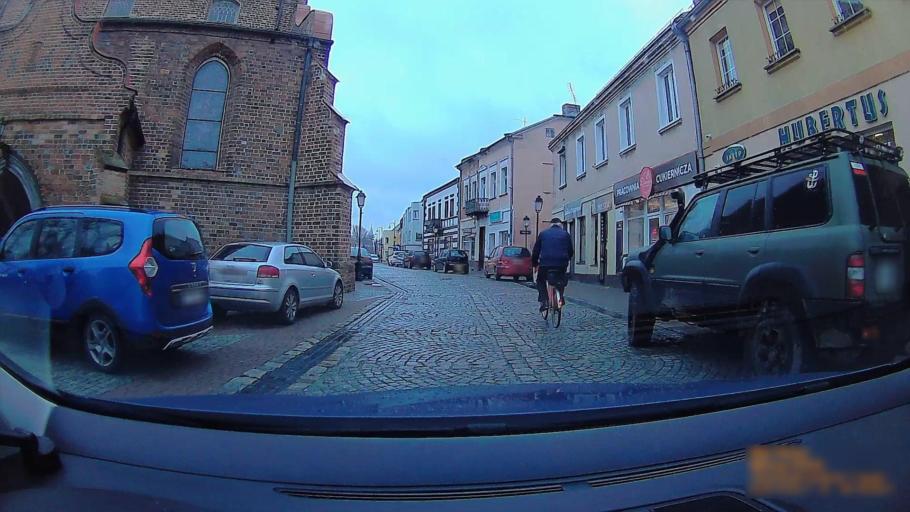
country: PL
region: Greater Poland Voivodeship
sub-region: Konin
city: Konin
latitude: 52.2094
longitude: 18.2545
